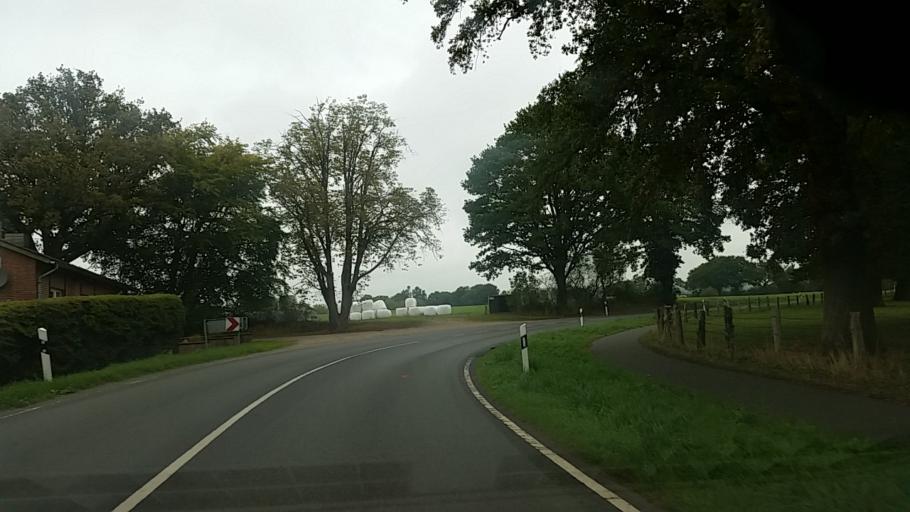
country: DE
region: Schleswig-Holstein
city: Schmalfeld
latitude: 53.8625
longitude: 9.9744
